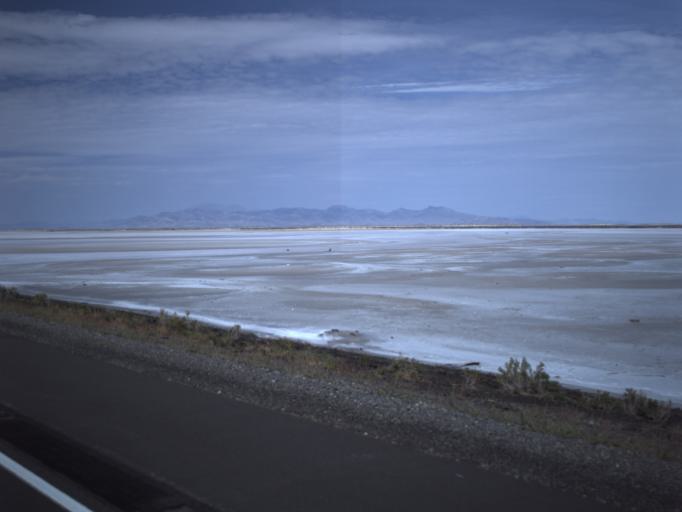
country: US
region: Utah
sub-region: Tooele County
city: Wendover
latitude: 40.7301
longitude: -113.4267
